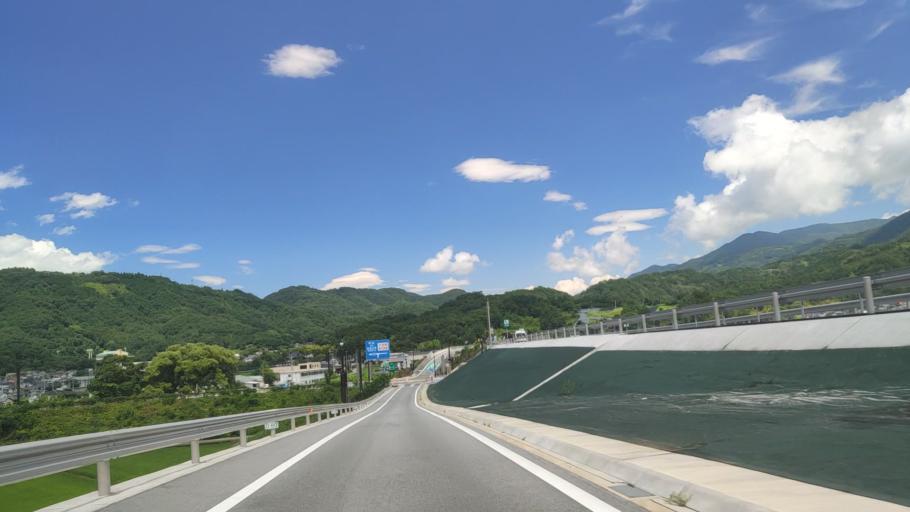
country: JP
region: Yamanashi
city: Ryuo
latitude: 35.4877
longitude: 138.4636
